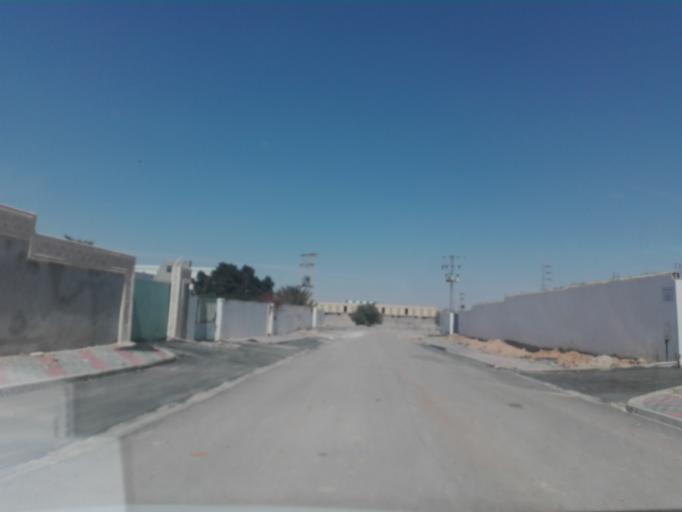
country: TN
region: Safaqis
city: Sfax
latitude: 34.7224
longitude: 10.5154
